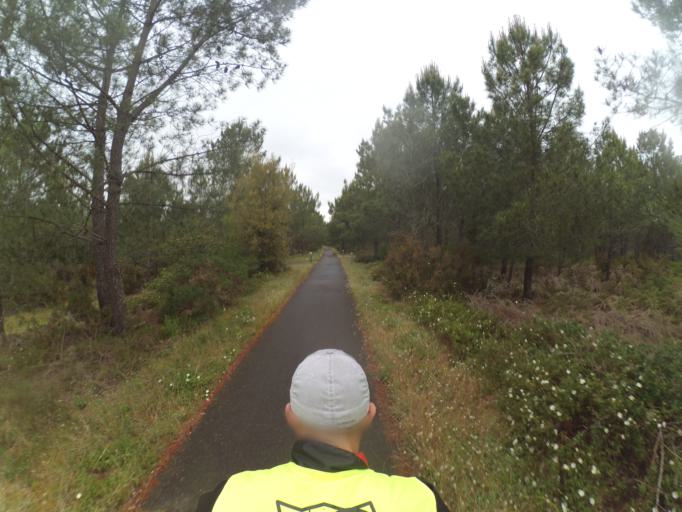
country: FR
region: Aquitaine
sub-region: Departement des Landes
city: Mimizan
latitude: 44.2238
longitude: -1.2588
